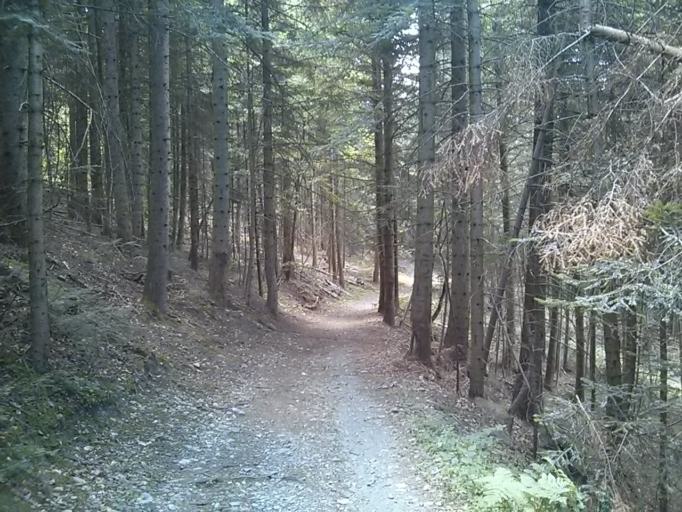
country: FR
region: Auvergne
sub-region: Departement de la Haute-Loire
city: Rosieres
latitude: 45.1015
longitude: 4.0409
